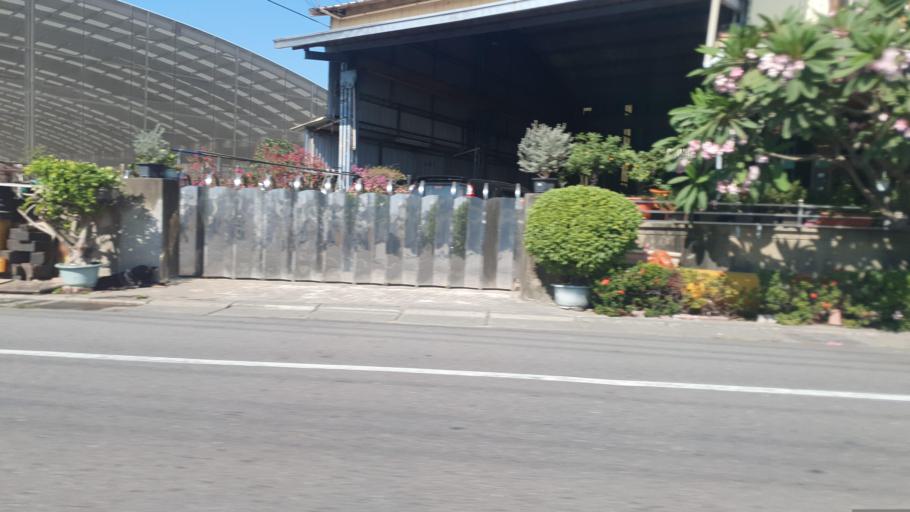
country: TW
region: Taiwan
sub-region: Tainan
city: Tainan
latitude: 23.0319
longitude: 120.2967
